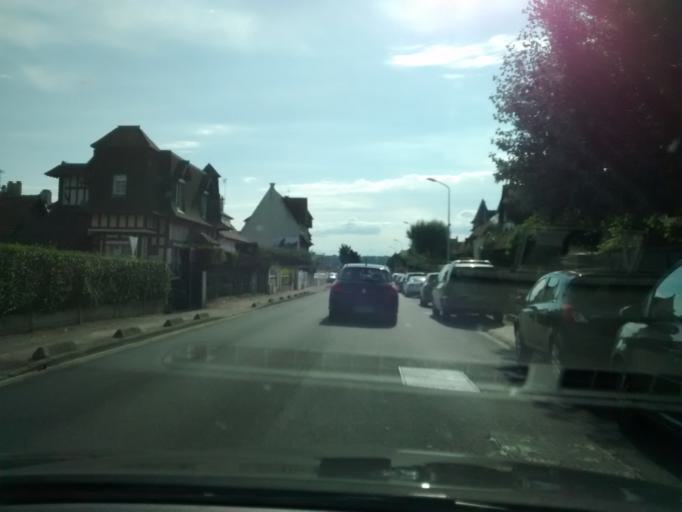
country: FR
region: Lower Normandy
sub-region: Departement du Calvados
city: Blonville-sur-Mer
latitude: 49.3373
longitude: 0.0244
